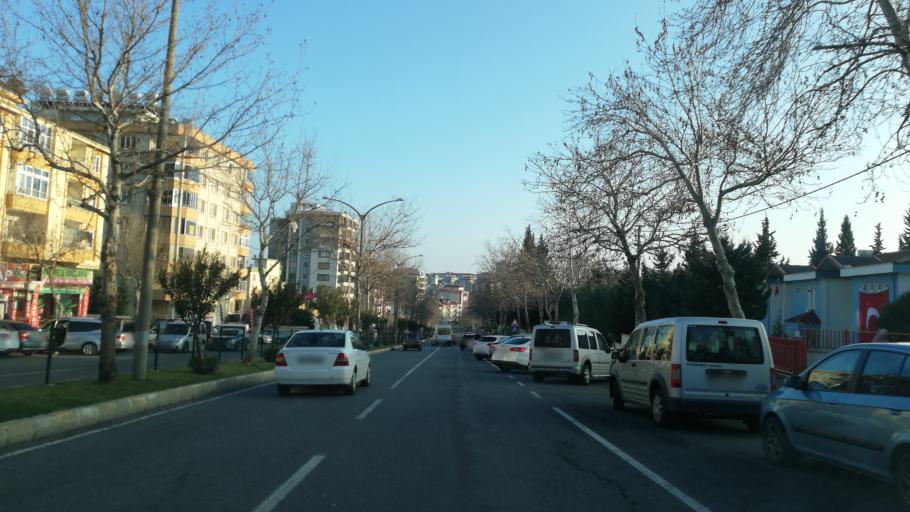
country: TR
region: Kahramanmaras
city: Kahramanmaras
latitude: 37.5894
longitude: 36.9028
